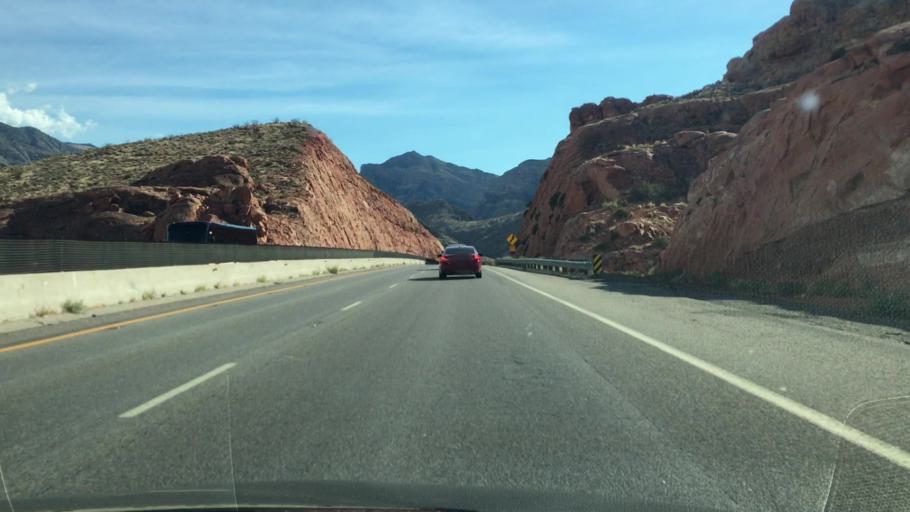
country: US
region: Arizona
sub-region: Mohave County
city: Beaver Dam
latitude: 36.9497
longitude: -113.8035
